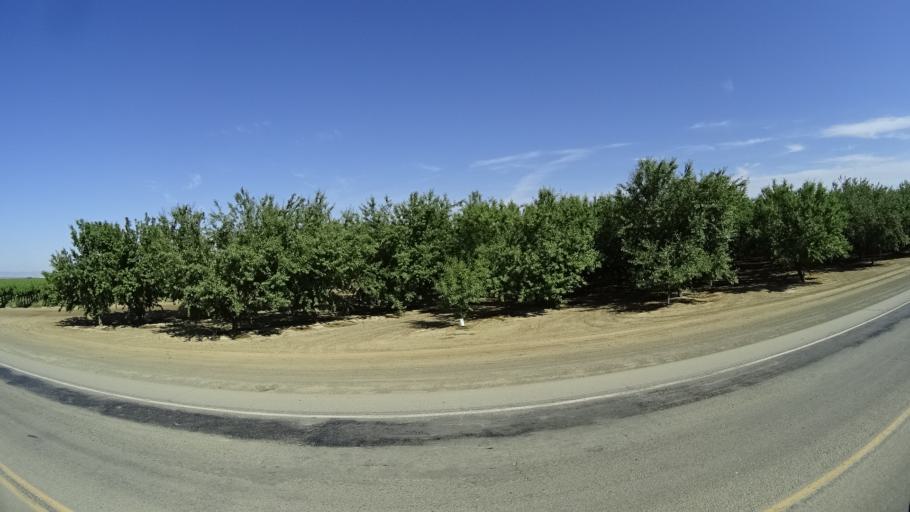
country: US
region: California
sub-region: Fresno County
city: Huron
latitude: 36.1438
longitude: -120.0037
